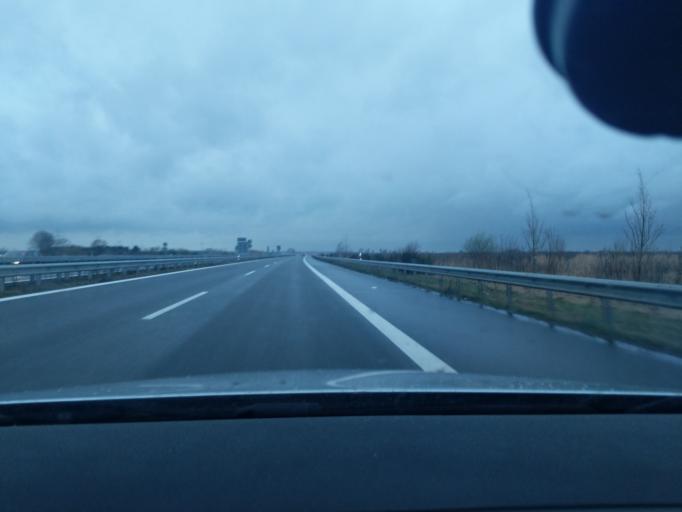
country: DE
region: Lower Saxony
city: Jork
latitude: 53.5037
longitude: 9.6506
